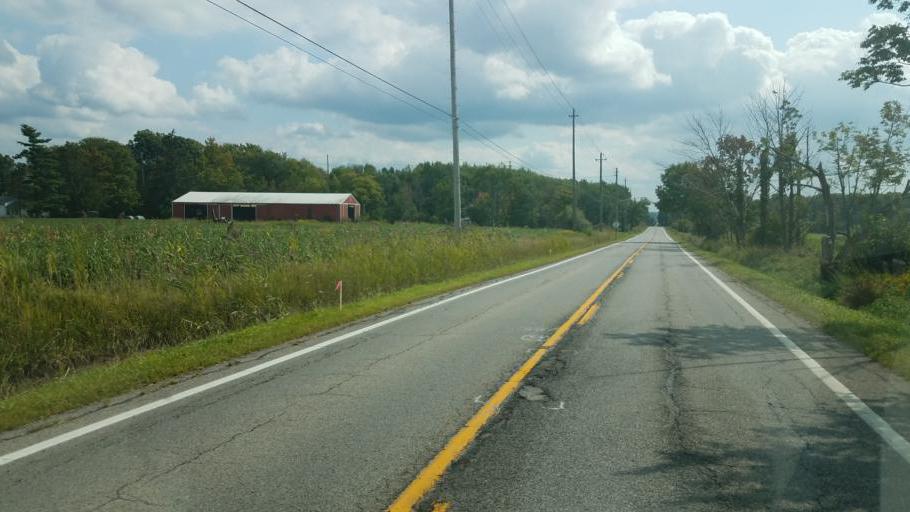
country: US
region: Ohio
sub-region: Geauga County
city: Burton
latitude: 41.4157
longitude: -81.2116
